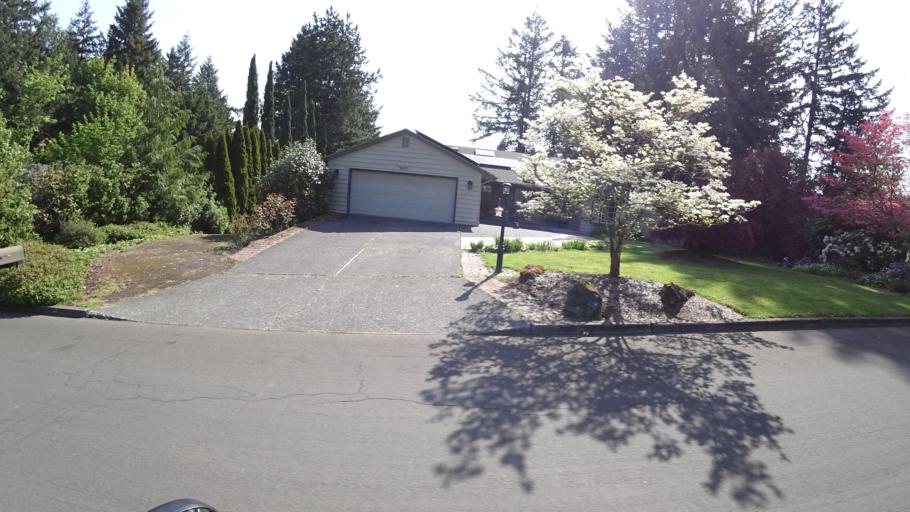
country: US
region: Oregon
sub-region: Washington County
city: Aloha
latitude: 45.4506
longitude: -122.8474
